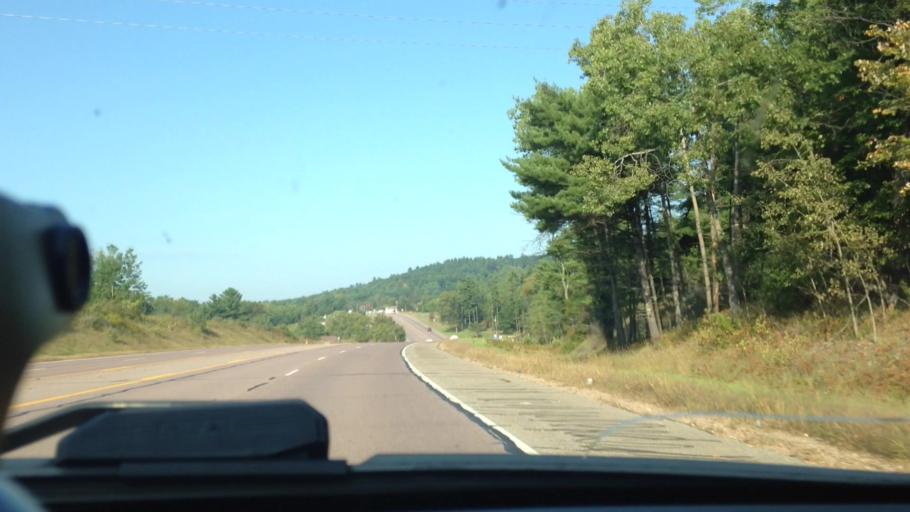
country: US
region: Michigan
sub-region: Dickinson County
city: Quinnesec
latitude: 45.8046
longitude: -87.9737
